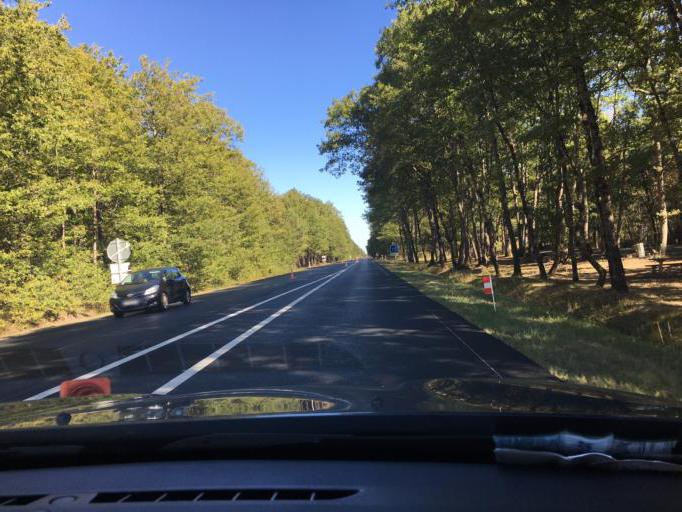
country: FR
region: Centre
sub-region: Departement d'Indre-et-Loire
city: Azay-le-Rideau
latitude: 47.2833
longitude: 0.5114
